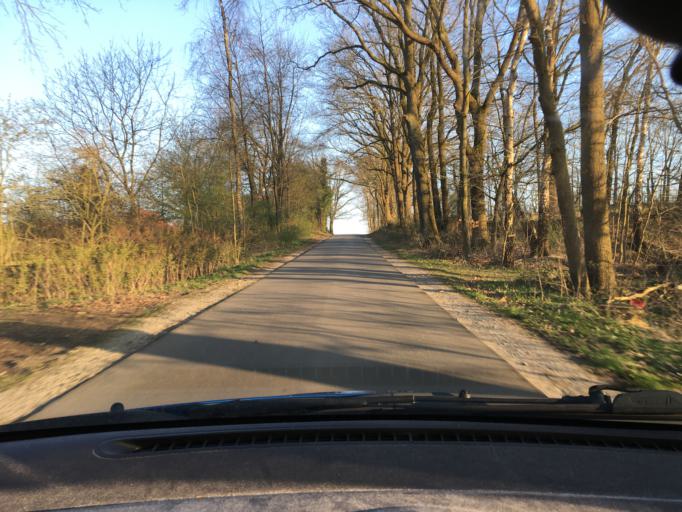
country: DE
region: Lower Saxony
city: Altenmedingen
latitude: 53.1746
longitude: 10.6360
